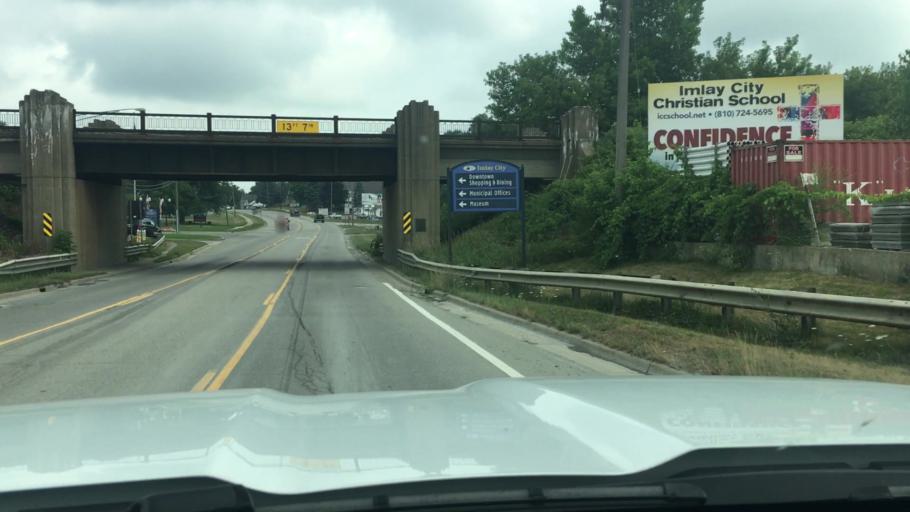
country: US
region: Michigan
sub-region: Lapeer County
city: Imlay City
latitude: 43.0228
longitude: -83.0718
